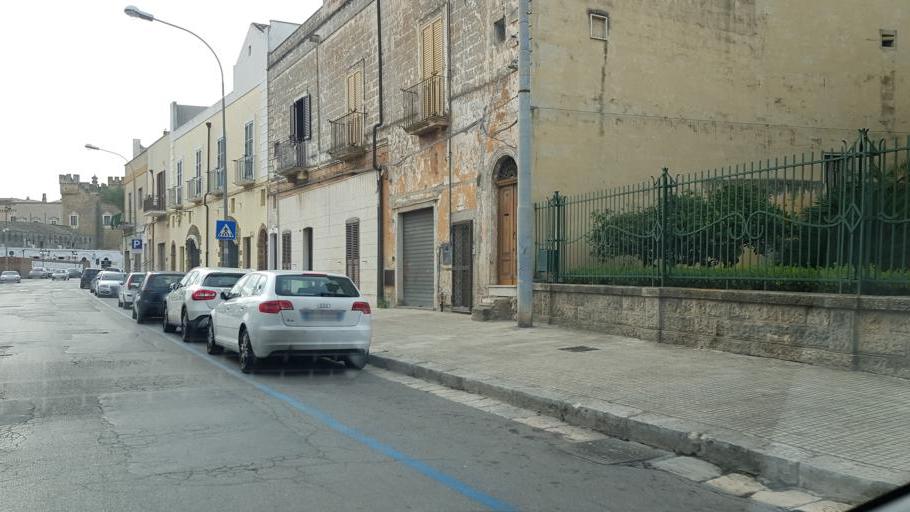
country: IT
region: Apulia
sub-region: Provincia di Brindisi
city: Mesagne
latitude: 40.5615
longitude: 17.8093
